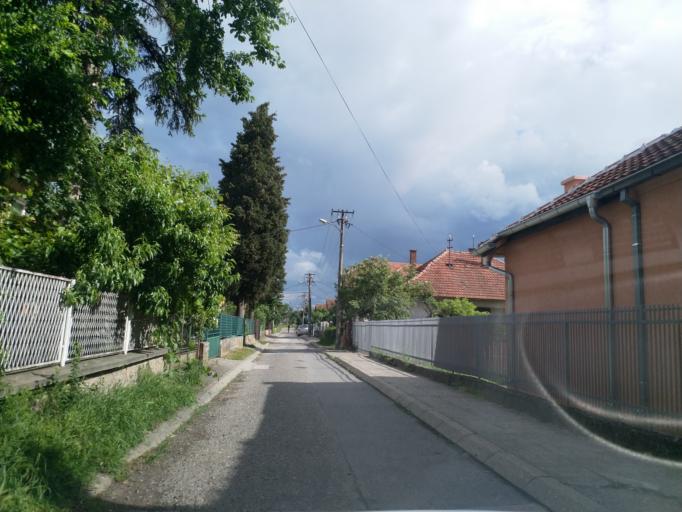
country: RS
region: Central Serbia
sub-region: Pomoravski Okrug
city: Paracin
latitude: 43.8575
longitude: 21.4157
